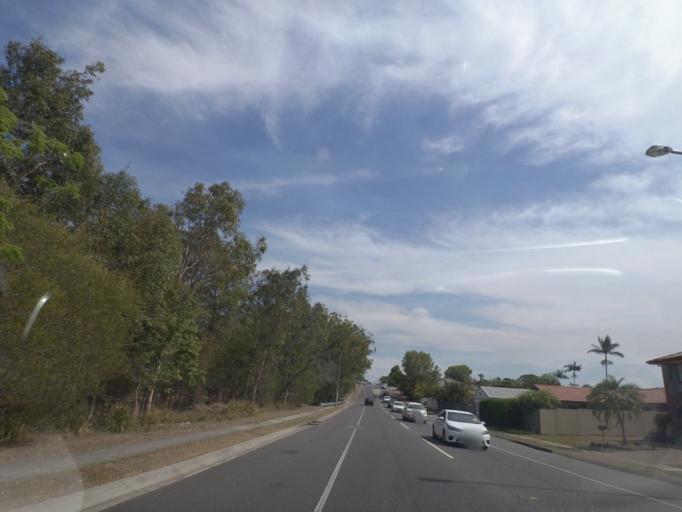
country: AU
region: Queensland
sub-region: Brisbane
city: Sunnybank Hills
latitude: -27.6079
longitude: 153.0627
